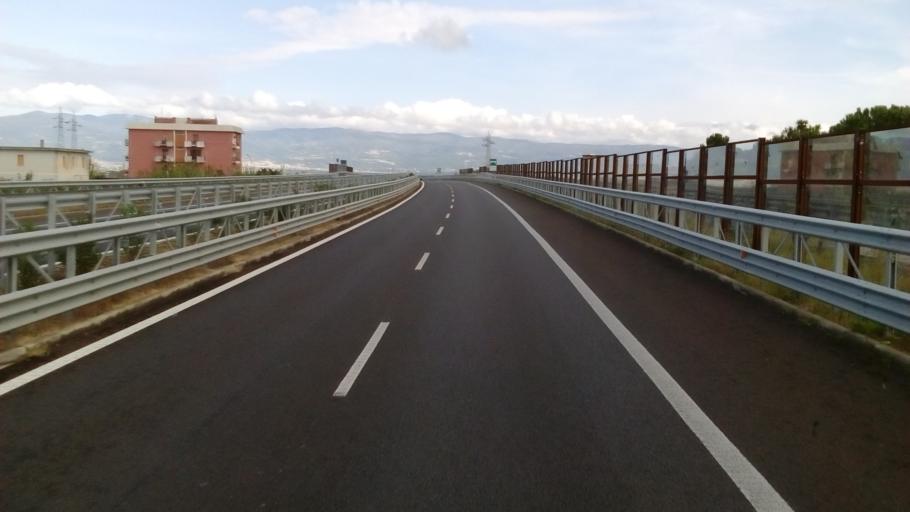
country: IT
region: Calabria
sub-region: Provincia di Catanzaro
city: Acconia
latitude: 38.8383
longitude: 16.2608
